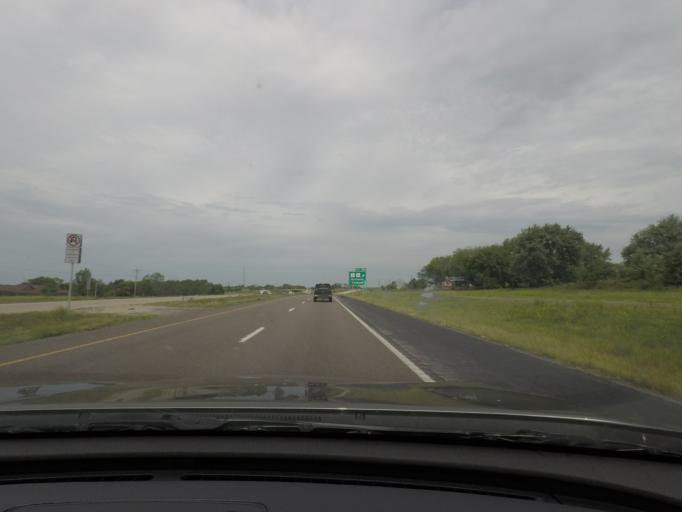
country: US
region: Missouri
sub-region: Callaway County
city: Fulton
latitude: 38.9323
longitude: -91.7997
